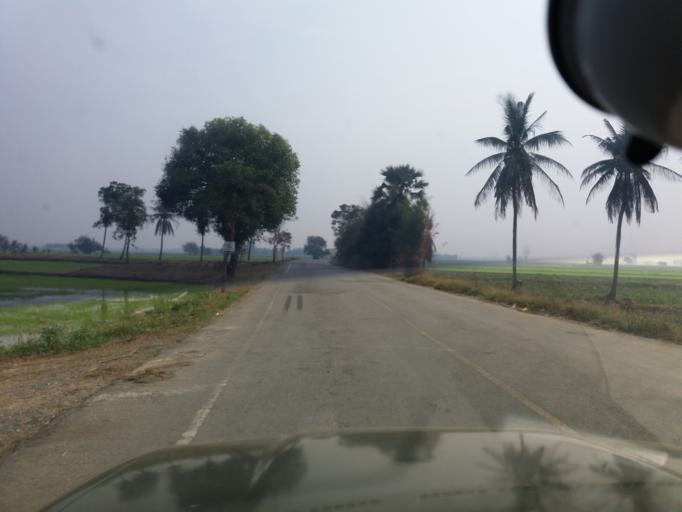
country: TH
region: Suphan Buri
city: Doem Bang Nang Buat
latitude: 14.8523
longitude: 100.1385
